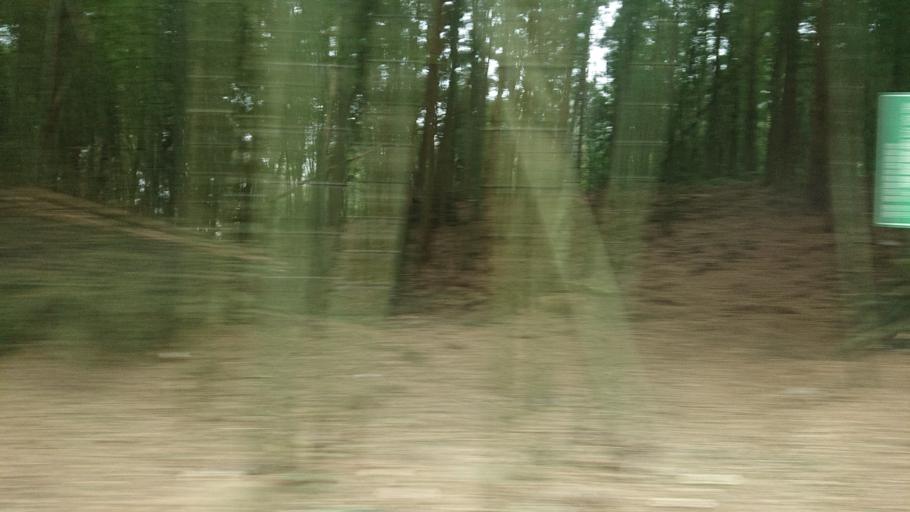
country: TW
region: Taiwan
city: Lugu
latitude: 23.6256
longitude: 120.7139
